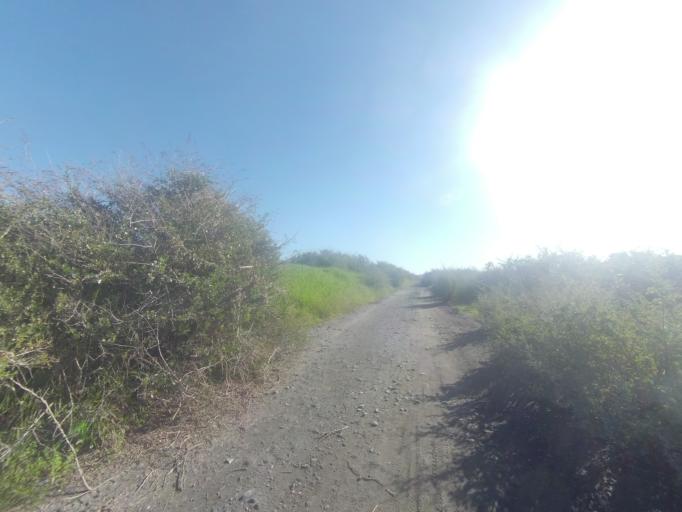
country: ES
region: Andalusia
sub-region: Provincia de Huelva
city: Palos de la Frontera
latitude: 37.2558
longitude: -6.9119
